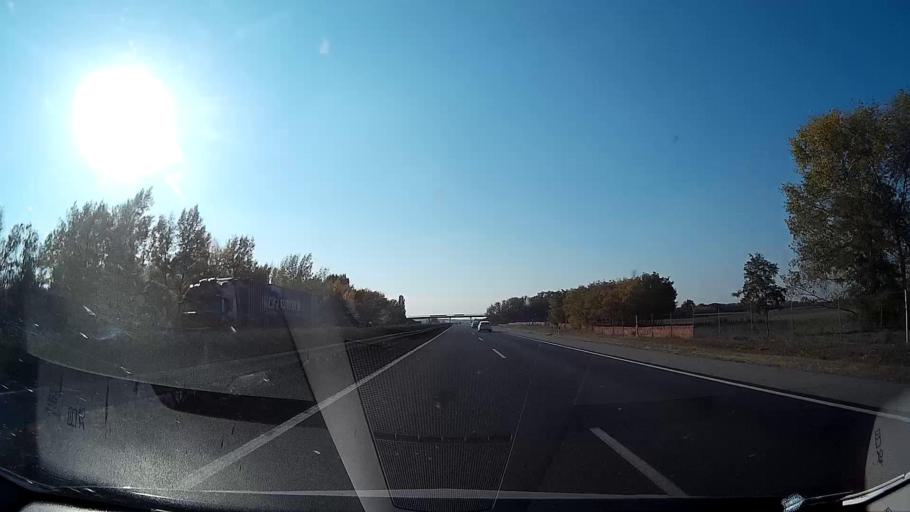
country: HU
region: Gyor-Moson-Sopron
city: Bony
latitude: 47.6848
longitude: 17.8665
